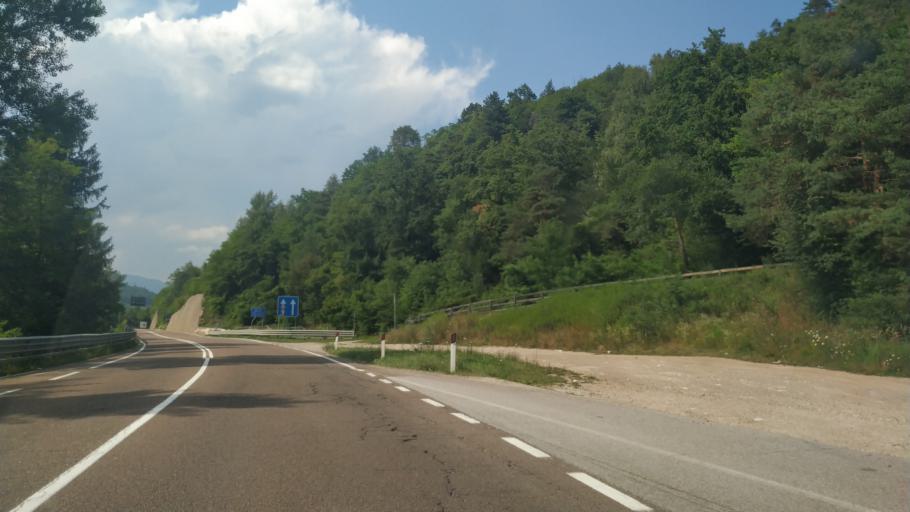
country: IT
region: Trentino-Alto Adige
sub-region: Provincia di Trento
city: Denno
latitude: 46.2779
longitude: 11.0647
